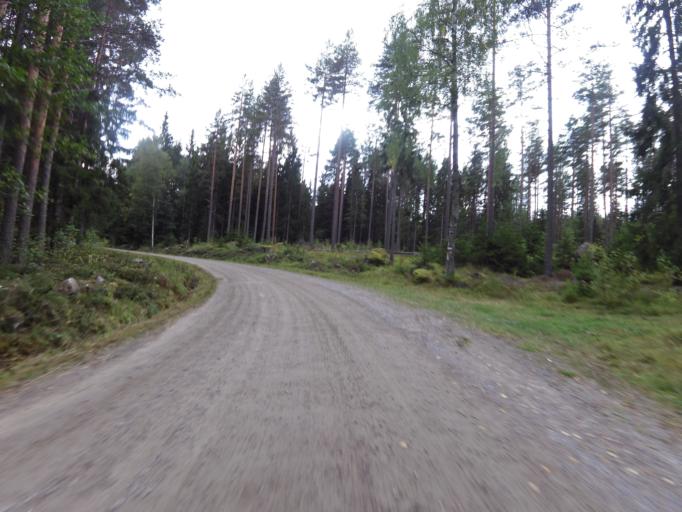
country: SE
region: Gaevleborg
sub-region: Sandvikens Kommun
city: Sandviken
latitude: 60.7468
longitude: 16.8397
